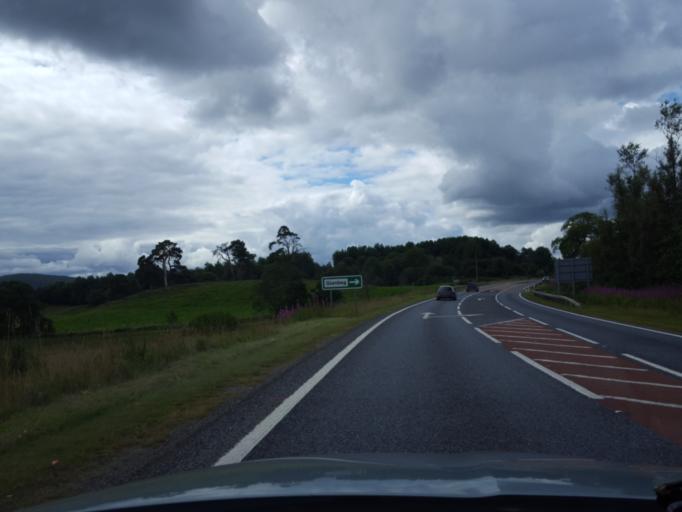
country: GB
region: Scotland
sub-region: Highland
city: Grantown on Spey
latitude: 57.3177
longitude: -3.6217
